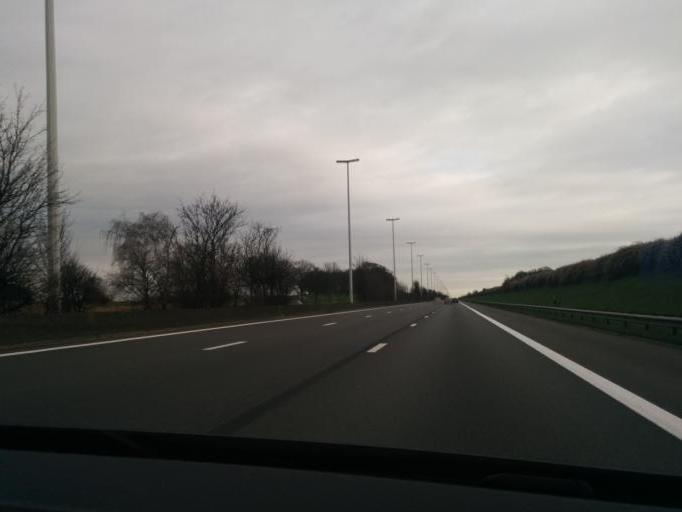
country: BE
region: Flanders
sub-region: Provincie Vlaams-Brabant
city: Bierbeek
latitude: 50.8355
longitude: 4.7742
